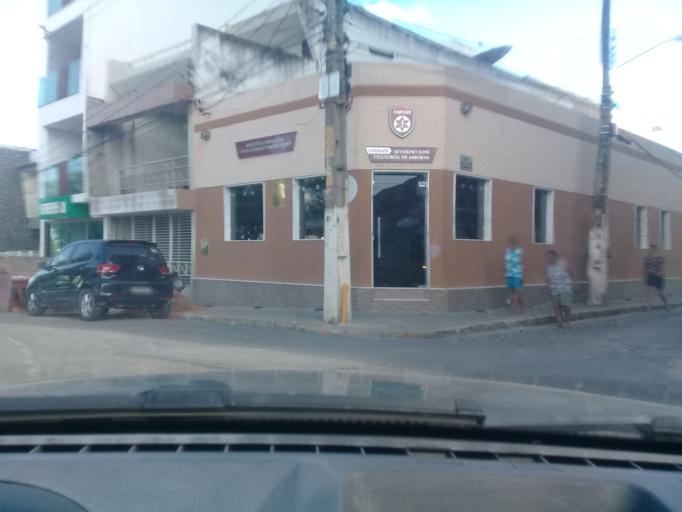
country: BR
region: Pernambuco
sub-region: Vitoria De Santo Antao
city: Vitoria de Santo Antao
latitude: -8.1201
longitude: -35.2992
